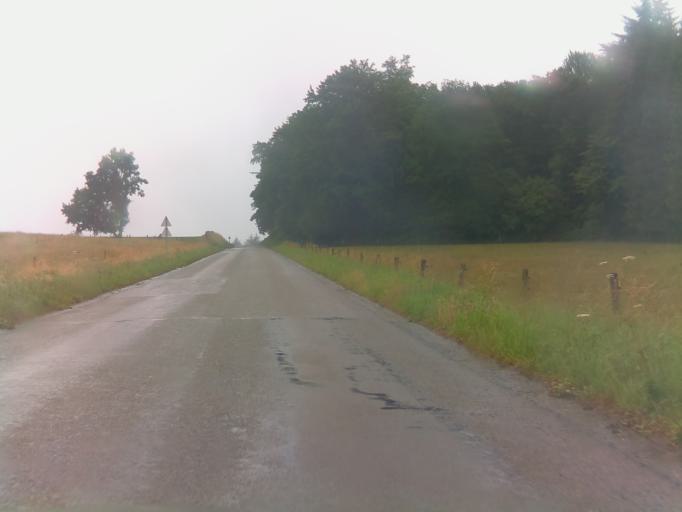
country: BE
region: Wallonia
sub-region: Province du Luxembourg
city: Paliseul
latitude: 49.9304
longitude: 5.0836
